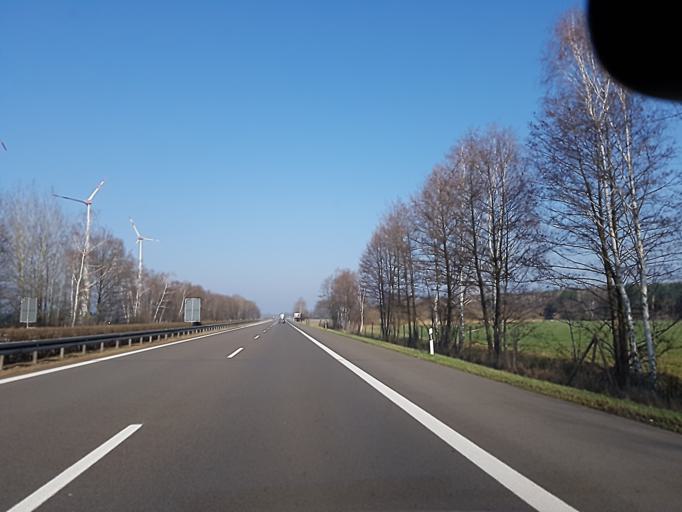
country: DE
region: Brandenburg
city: Forst
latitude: 51.7023
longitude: 14.6485
